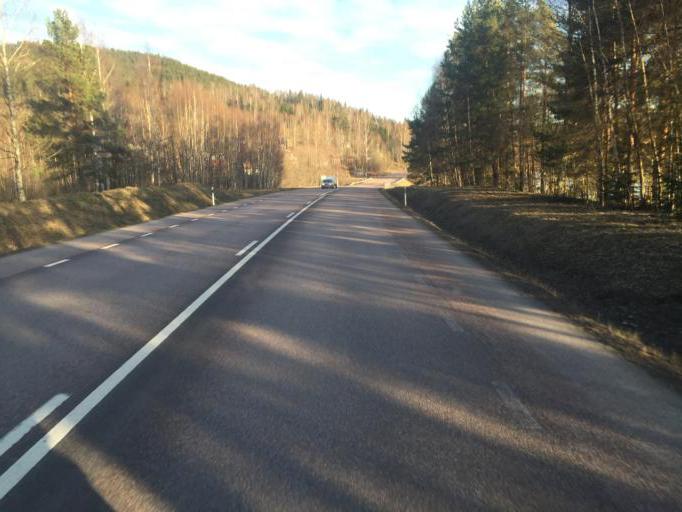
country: SE
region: Dalarna
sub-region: Gagnefs Kommun
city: Djuras
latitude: 60.5468
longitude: 15.2758
